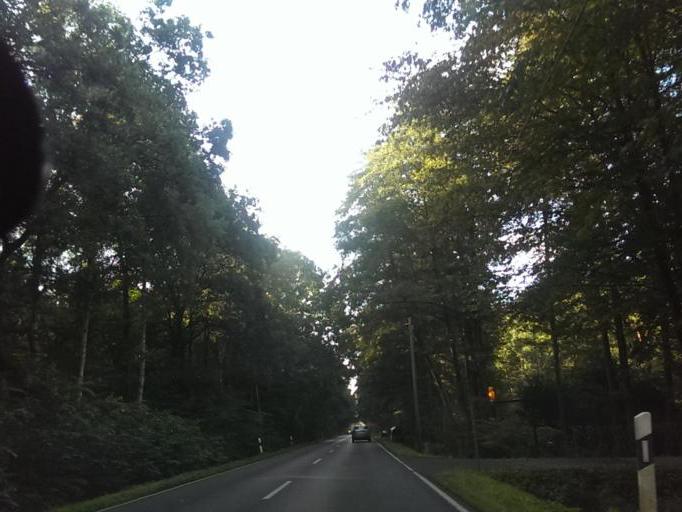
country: DE
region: Lower Saxony
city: Garbsen-Mitte
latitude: 52.4896
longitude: 9.6344
